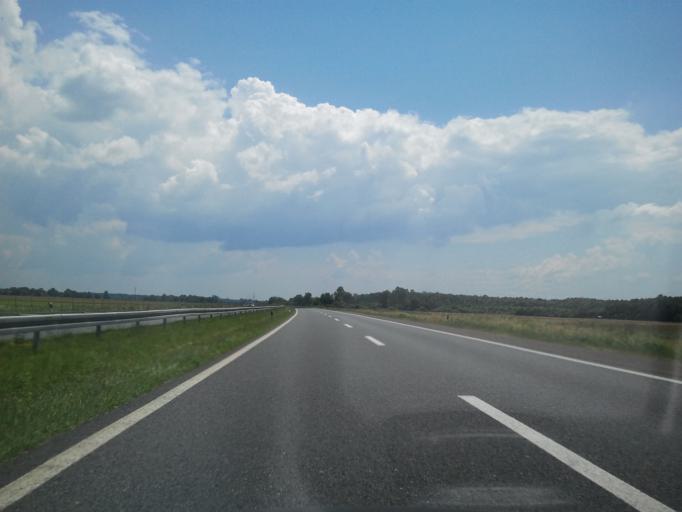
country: HR
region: Sisacko-Moslavacka
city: Lipovljani
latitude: 45.3751
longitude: 16.8793
